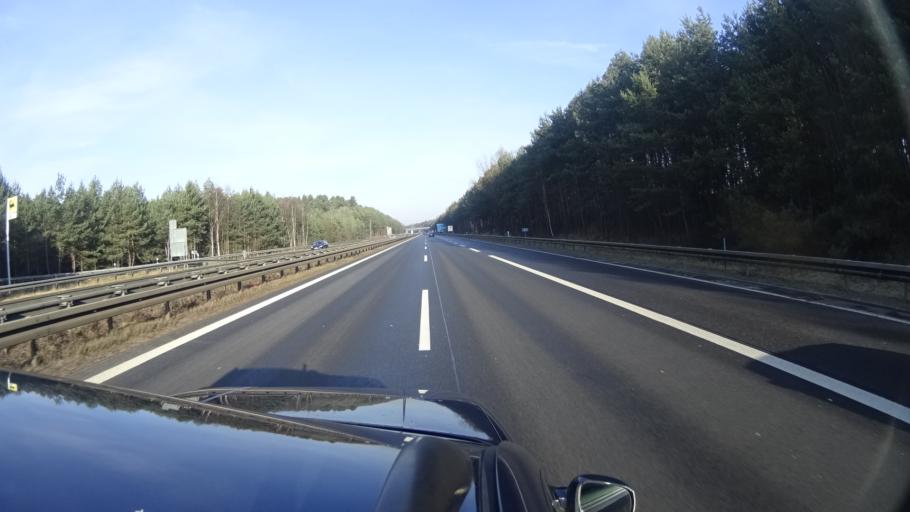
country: DE
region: Berlin
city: Heiligensee
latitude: 52.6470
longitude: 13.2431
